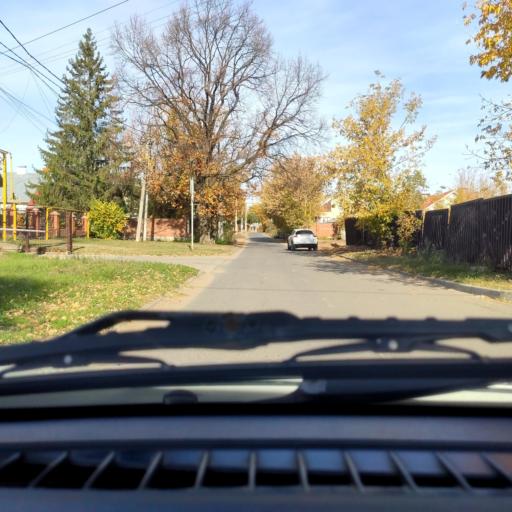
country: RU
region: Samara
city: Tol'yatti
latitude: 53.5315
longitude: 49.3894
